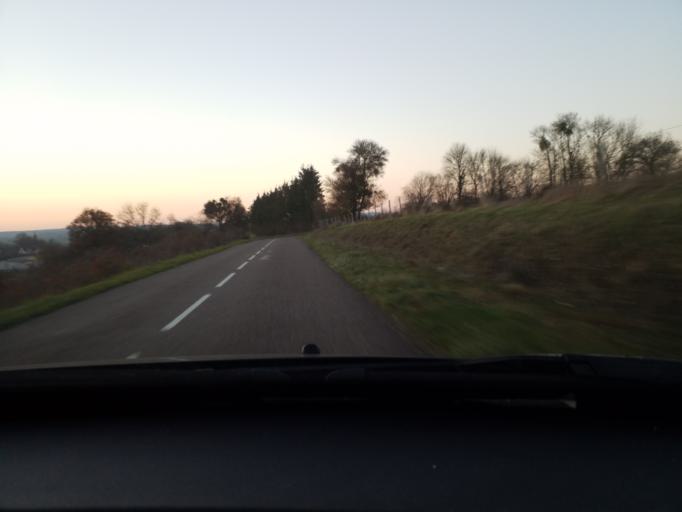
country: FR
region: Franche-Comte
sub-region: Departement de la Haute-Saone
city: Faverney
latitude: 47.8839
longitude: 6.1392
